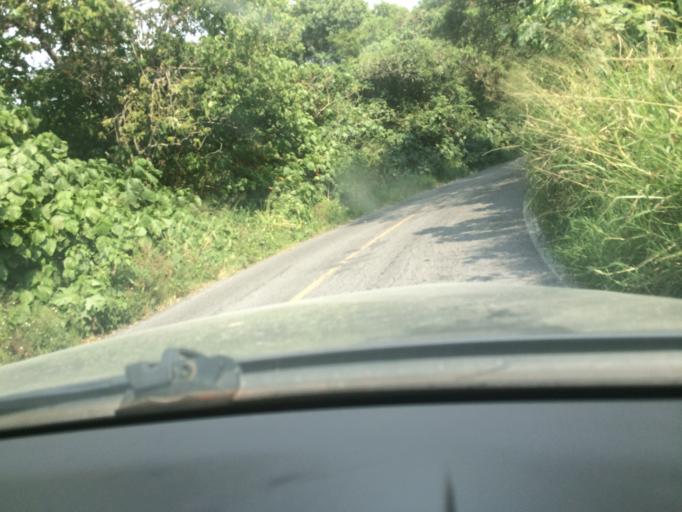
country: MX
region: Colima
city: Suchitlan
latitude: 19.4743
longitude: -103.6802
